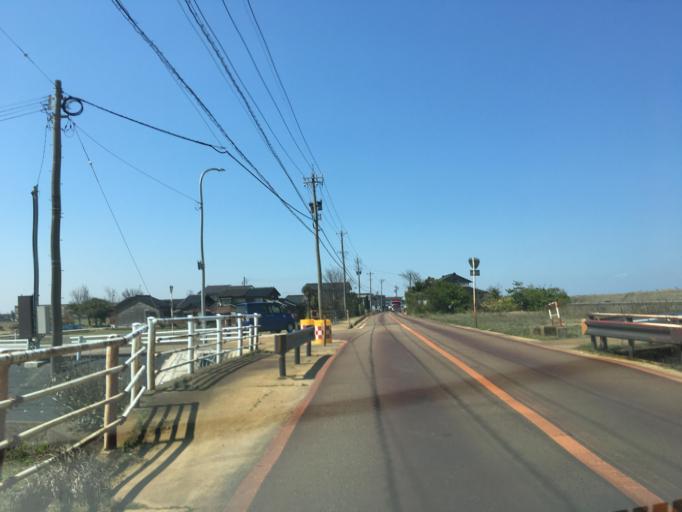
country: JP
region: Toyama
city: Kuragaki-kosugi
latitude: 36.7569
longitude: 137.1826
